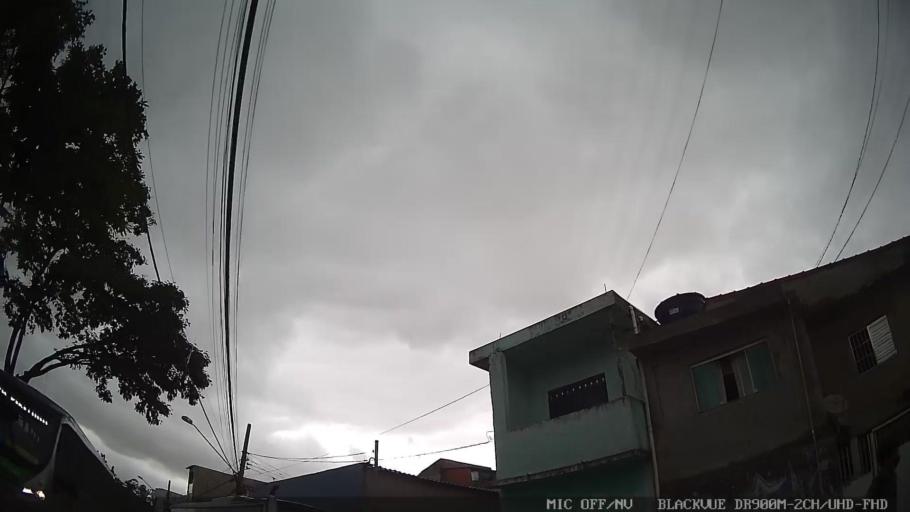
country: BR
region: Sao Paulo
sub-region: Osasco
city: Osasco
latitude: -23.4695
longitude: -46.7136
